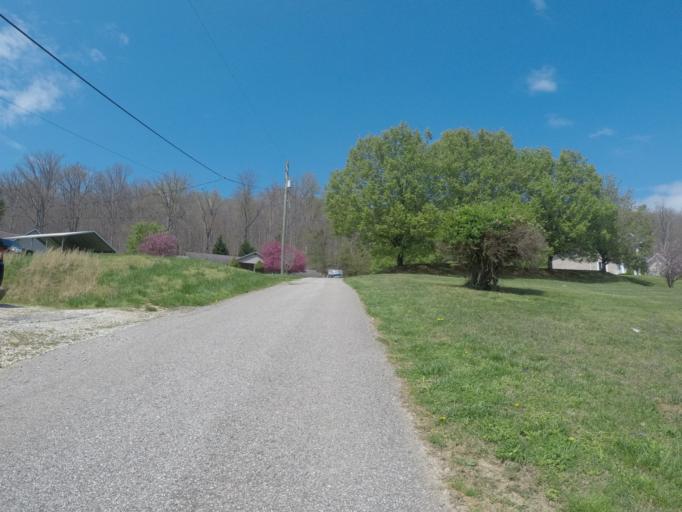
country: US
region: Ohio
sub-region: Lawrence County
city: Burlington
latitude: 38.3854
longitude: -82.5210
